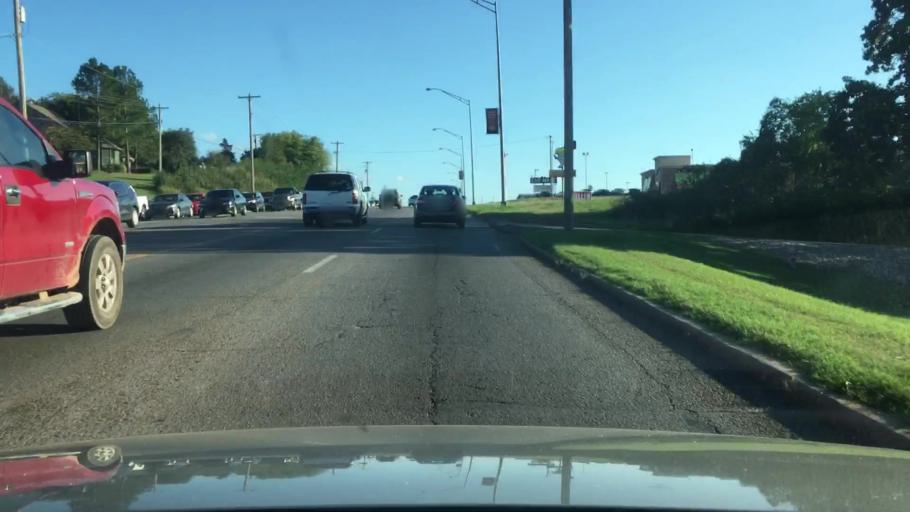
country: US
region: Oklahoma
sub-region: Cherokee County
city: Park Hill
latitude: 35.8856
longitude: -94.9767
